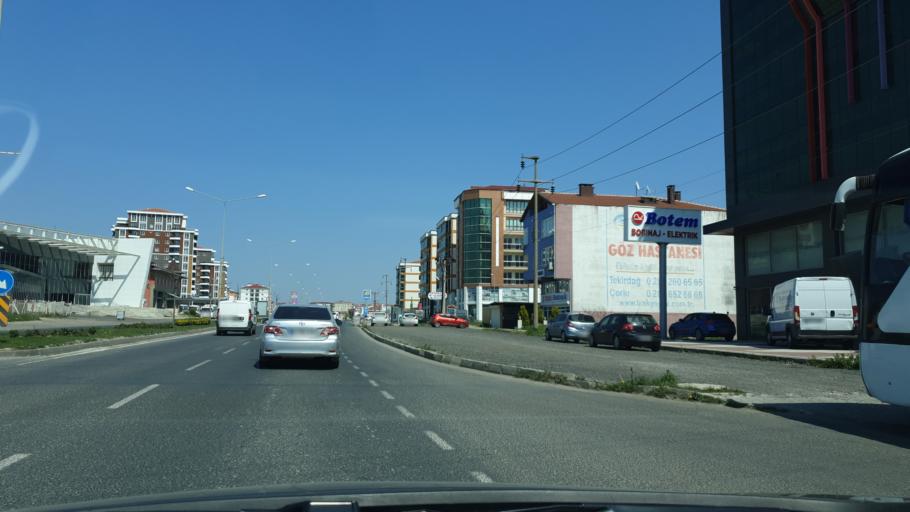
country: TR
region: Tekirdag
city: Corlu
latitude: 41.1527
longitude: 27.7793
